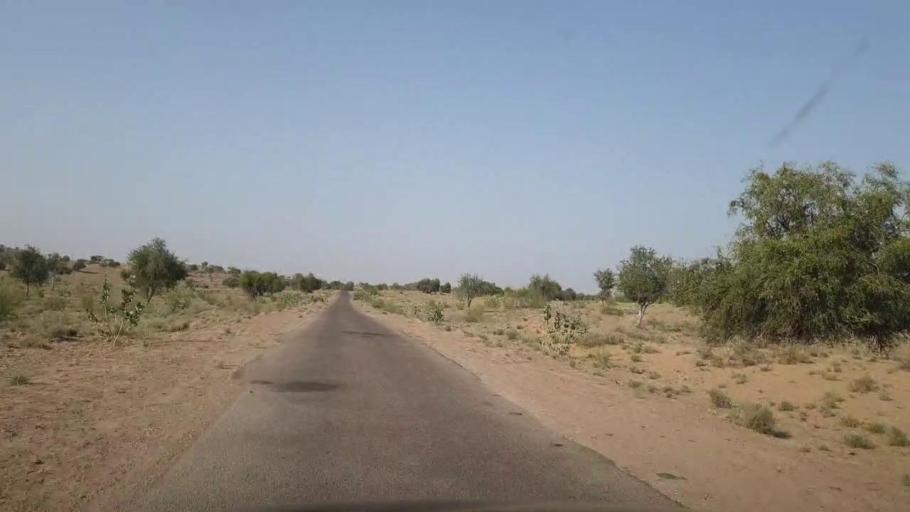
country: PK
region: Sindh
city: Islamkot
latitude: 25.1426
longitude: 70.5187
